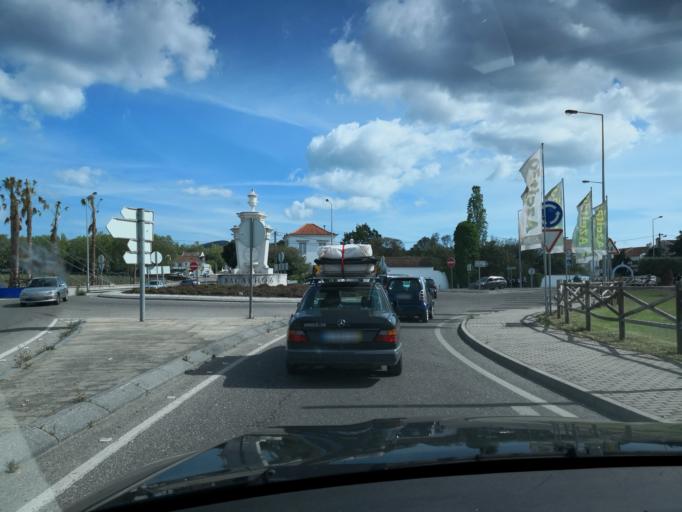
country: PT
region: Setubal
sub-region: Palmela
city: Quinta do Anjo
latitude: 38.5221
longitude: -9.0160
